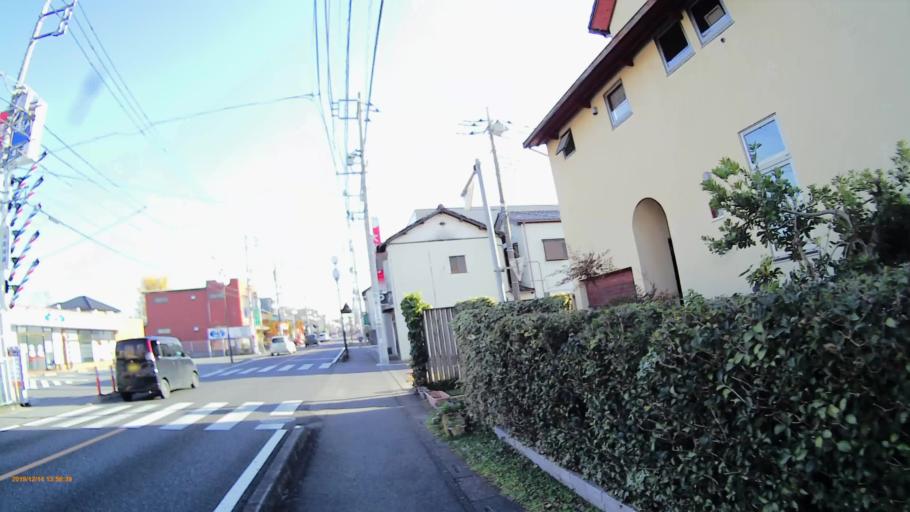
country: JP
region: Saitama
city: Konosu
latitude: 36.0635
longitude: 139.5091
